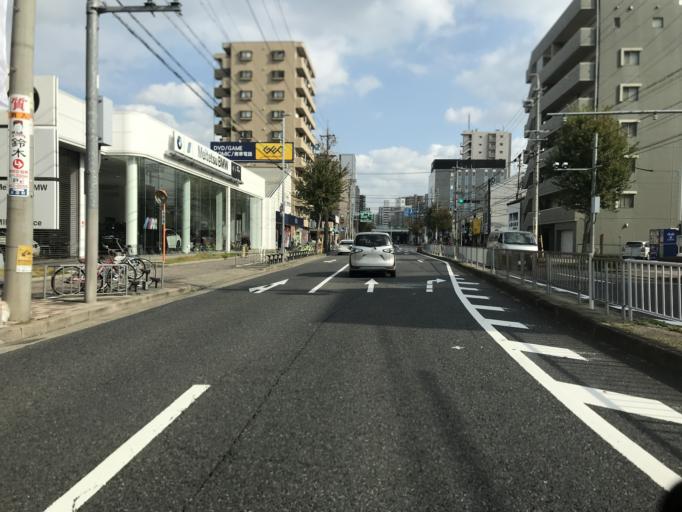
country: JP
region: Aichi
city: Nagoya-shi
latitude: 35.1753
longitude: 136.8775
